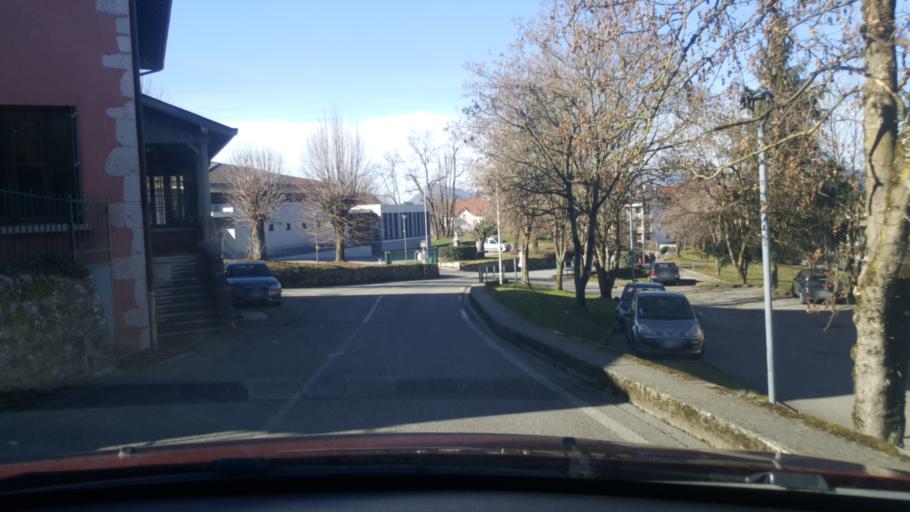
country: FR
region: Rhone-Alpes
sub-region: Departement de la Haute-Savoie
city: Annecy
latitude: 45.8934
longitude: 6.1282
